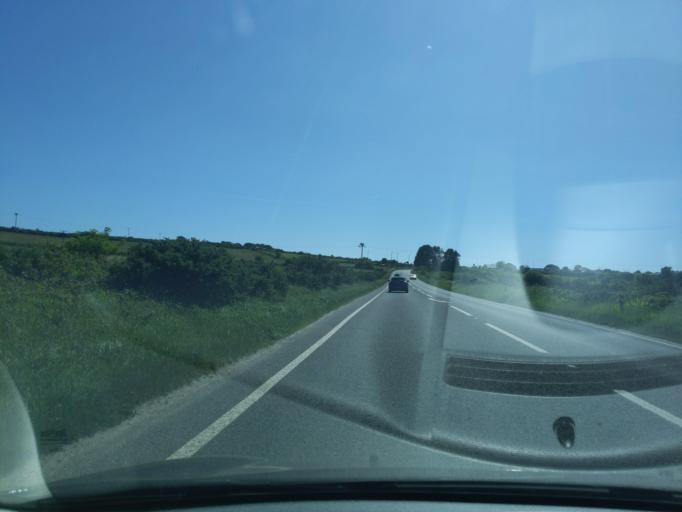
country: GB
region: England
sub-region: Cornwall
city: Penryn
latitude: 50.1664
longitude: -5.1518
